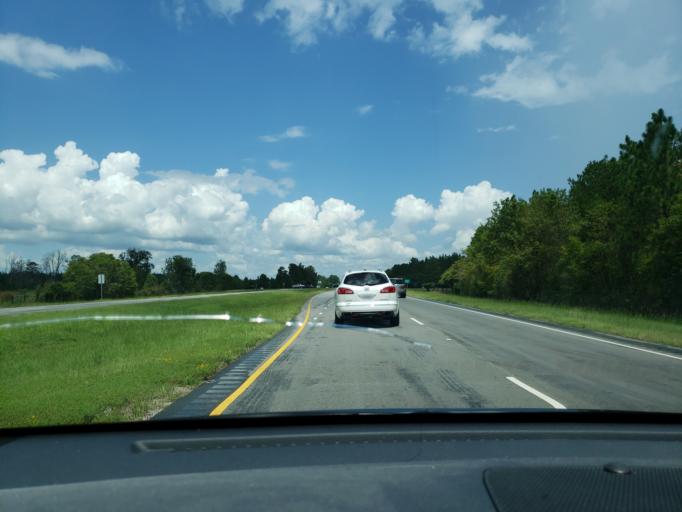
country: US
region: North Carolina
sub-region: Robeson County
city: Saint Pauls
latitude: 34.8439
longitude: -78.8553
